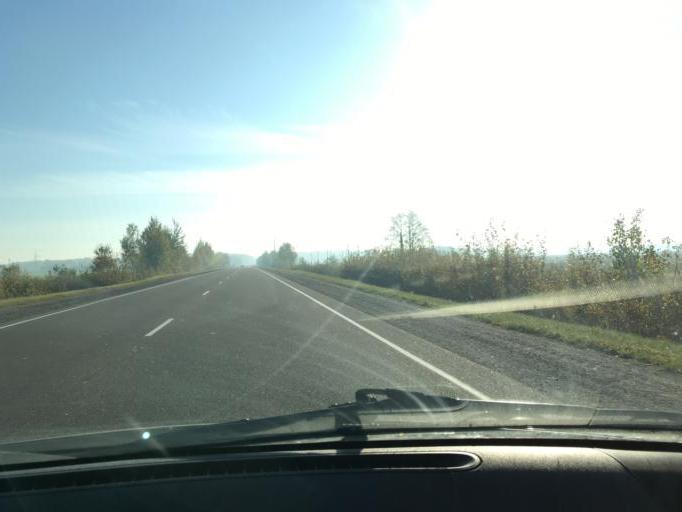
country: BY
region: Brest
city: Horad Luninyets
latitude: 52.3130
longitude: 26.6547
